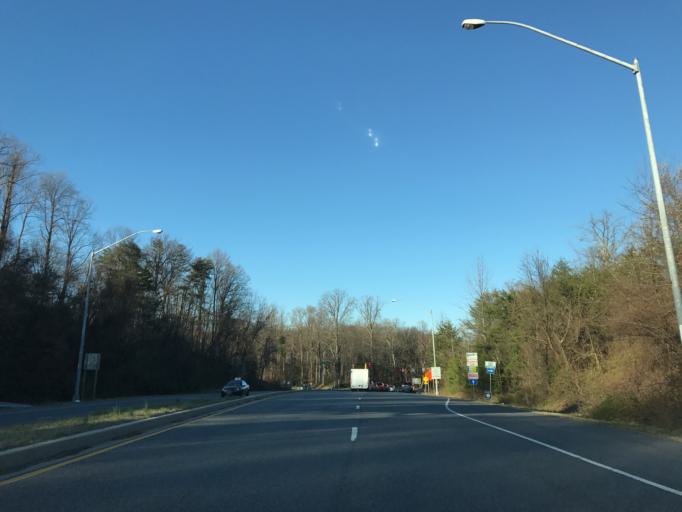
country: US
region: Maryland
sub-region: Anne Arundel County
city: Cape Saint Claire
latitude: 39.0291
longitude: -76.4478
